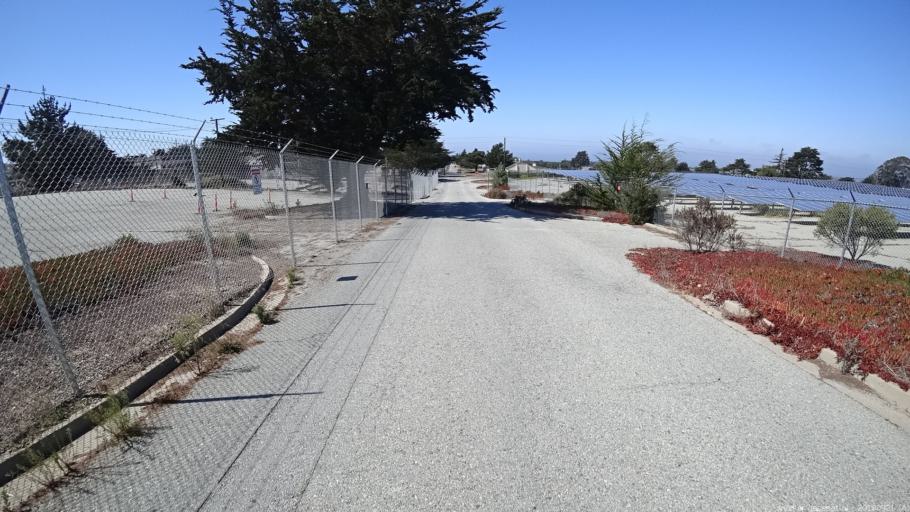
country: US
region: California
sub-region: Monterey County
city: Marina
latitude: 36.6463
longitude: -121.7887
